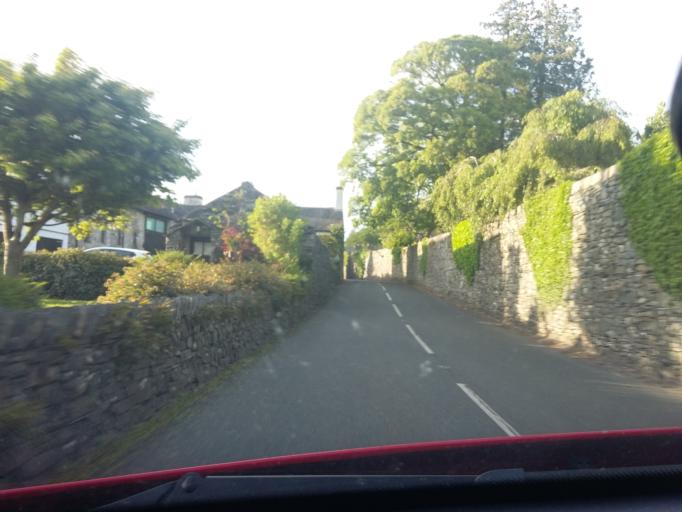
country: GB
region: England
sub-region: Cumbria
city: Windermere
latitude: 54.3937
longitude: -2.9152
